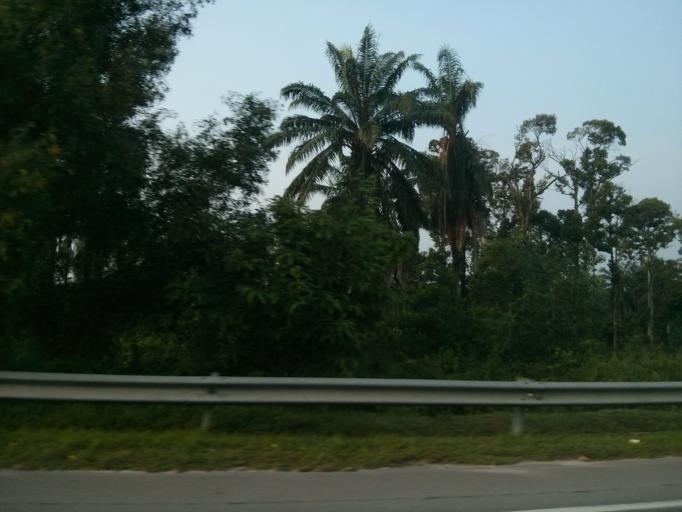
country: MY
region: Putrajaya
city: Putrajaya
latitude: 2.8696
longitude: 101.6858
